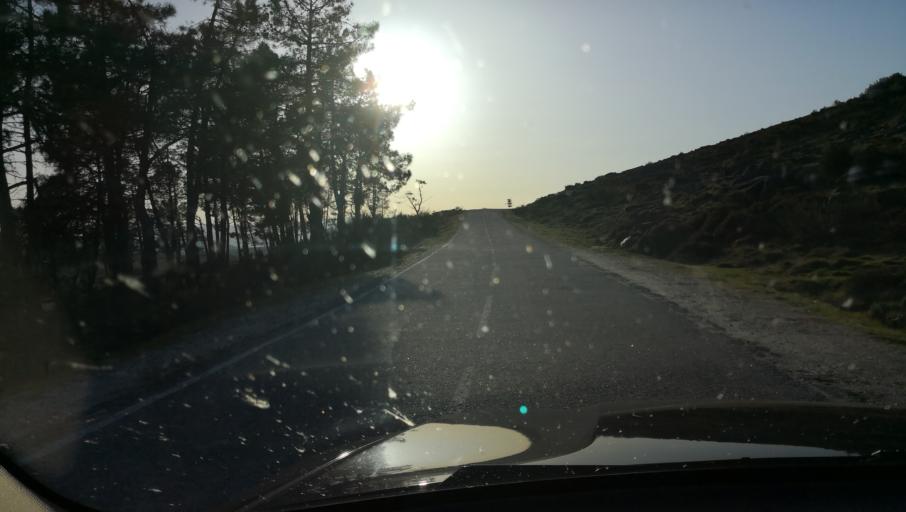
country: PT
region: Vila Real
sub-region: Vila Real
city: Vila Real
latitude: 41.3806
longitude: -7.8183
